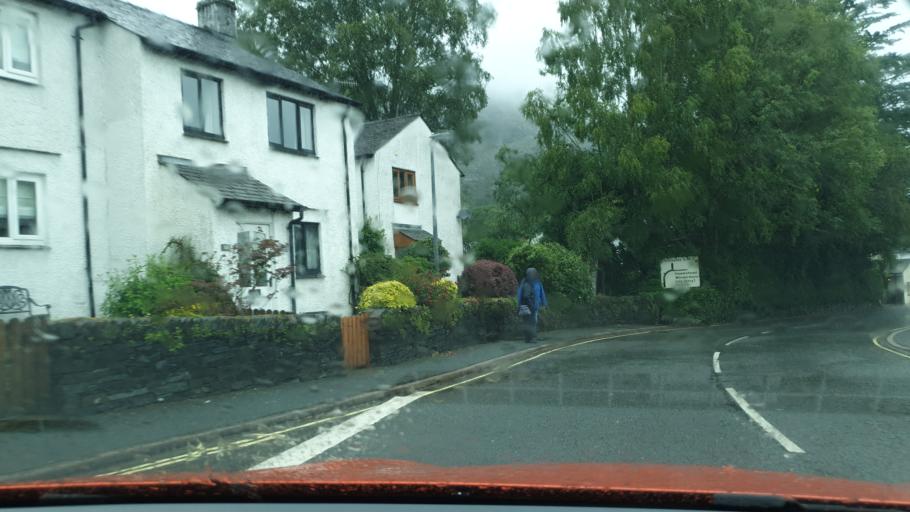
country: GB
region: England
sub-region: Cumbria
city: Ambleside
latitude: 54.3682
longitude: -3.0766
